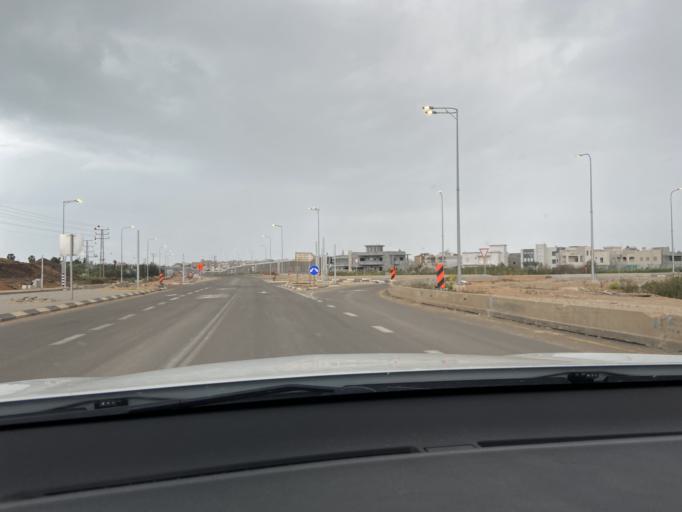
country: IL
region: Northern District
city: El Mazra`a
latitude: 32.9795
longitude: 35.1072
